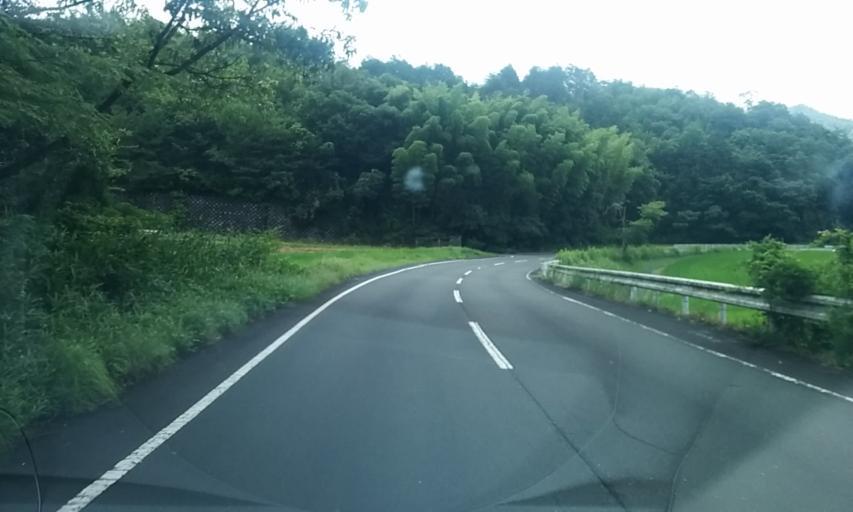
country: JP
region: Kyoto
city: Kameoka
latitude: 35.0895
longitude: 135.4349
